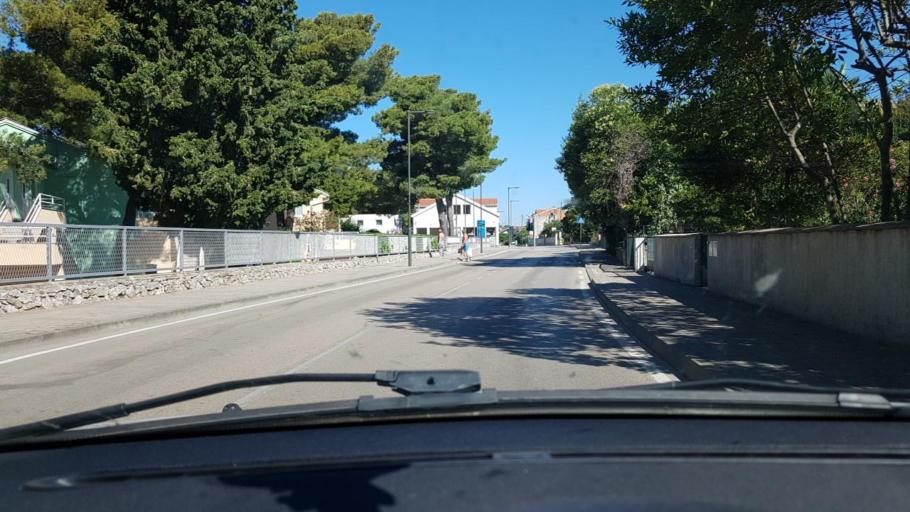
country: HR
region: Sibensko-Kniniska
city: Vodice
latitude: 43.7572
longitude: 15.7852
